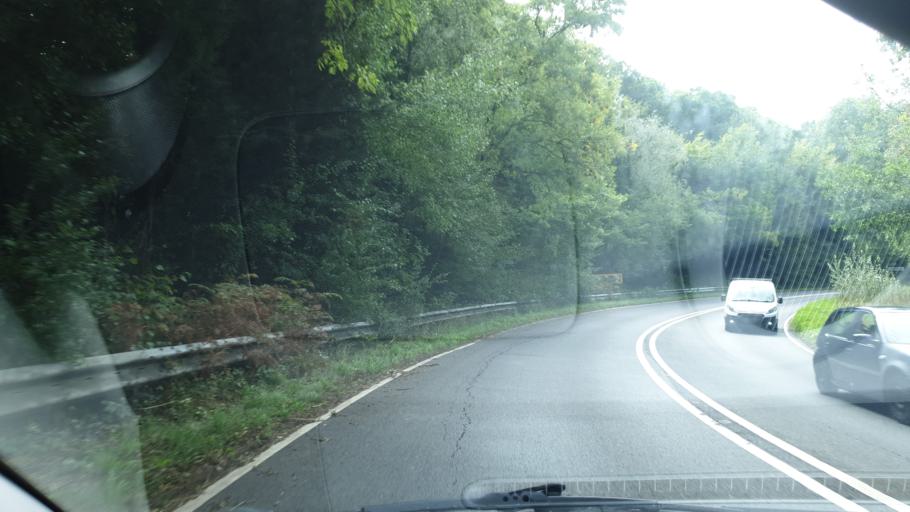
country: GB
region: England
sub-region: East Sussex
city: Forest Row
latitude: 51.1089
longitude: 0.0257
